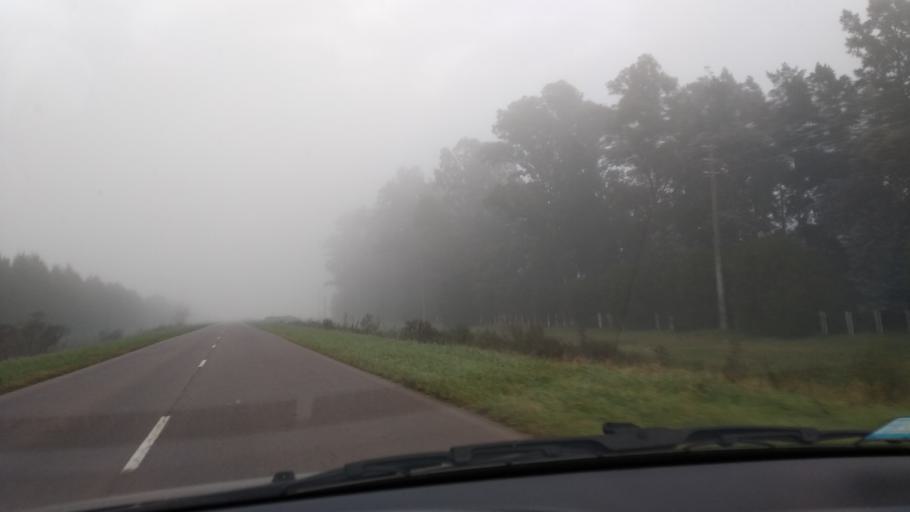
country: AR
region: Buenos Aires
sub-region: Partido de San Vicente
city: San Vicente
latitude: -35.2461
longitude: -58.4861
